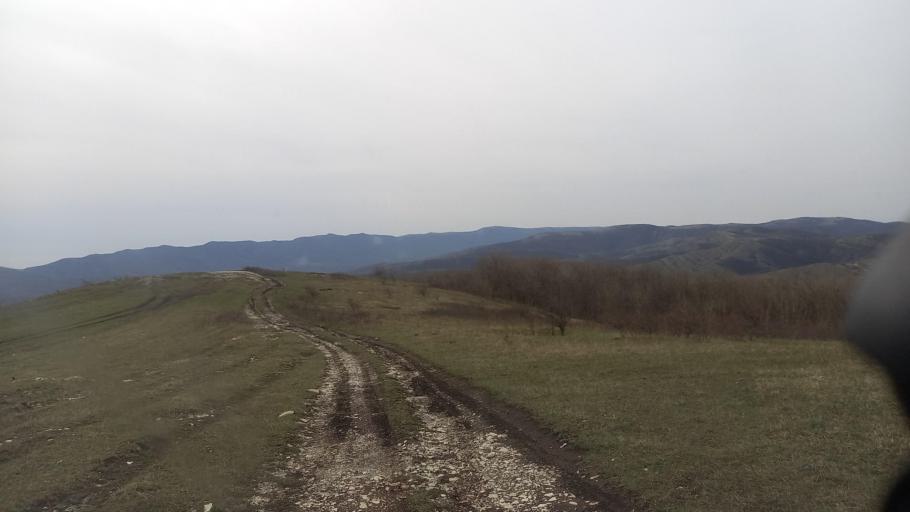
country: RU
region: Krasnodarskiy
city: Divnomorskoye
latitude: 44.5955
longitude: 38.2421
